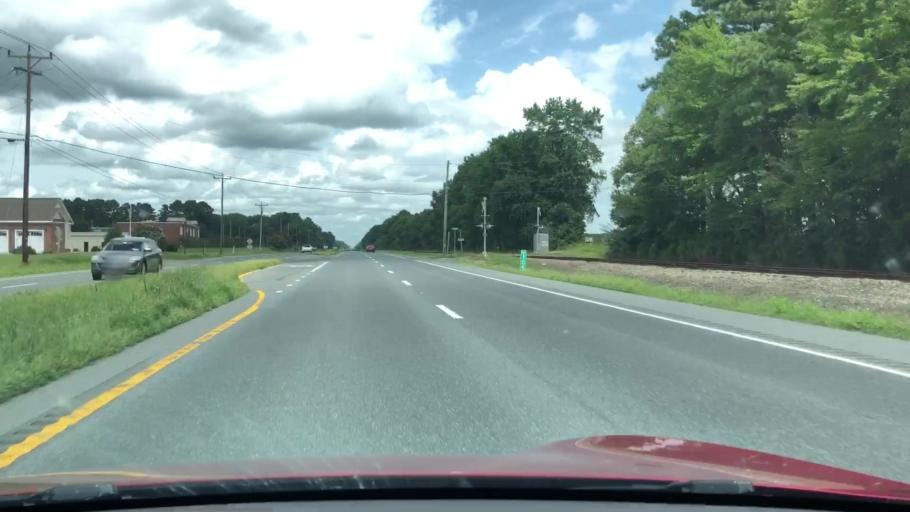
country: US
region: Virginia
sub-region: Northampton County
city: Exmore
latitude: 37.5968
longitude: -75.7777
